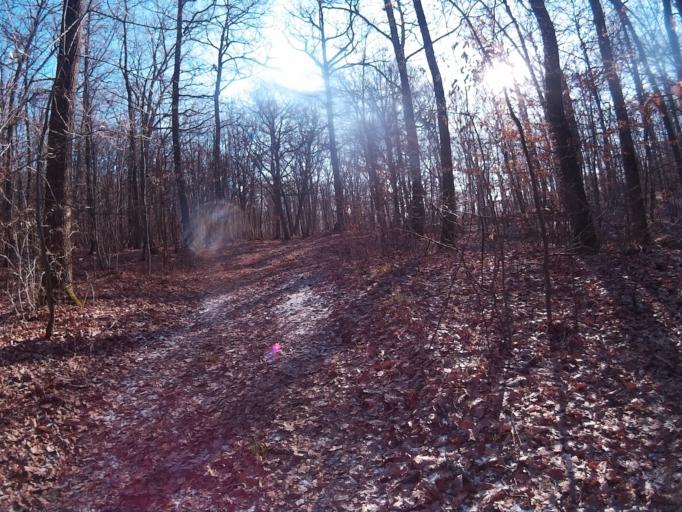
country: HU
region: Borsod-Abauj-Zemplen
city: Rudabanya
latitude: 48.4898
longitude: 20.5751
